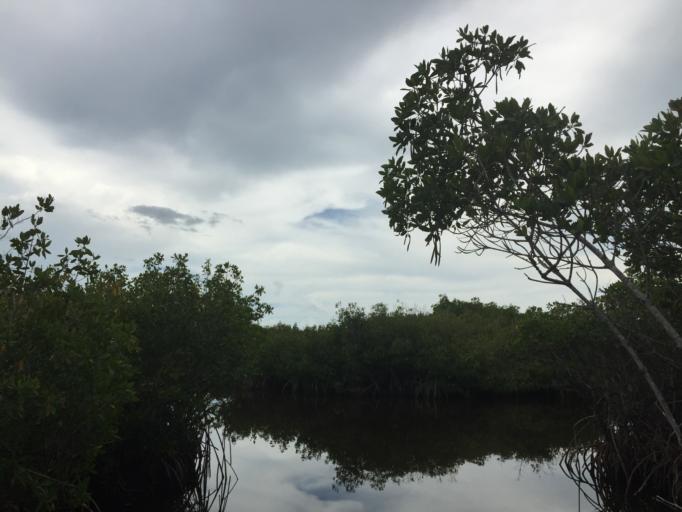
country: US
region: Florida
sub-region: Collier County
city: Marco
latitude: 25.9011
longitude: -81.3738
